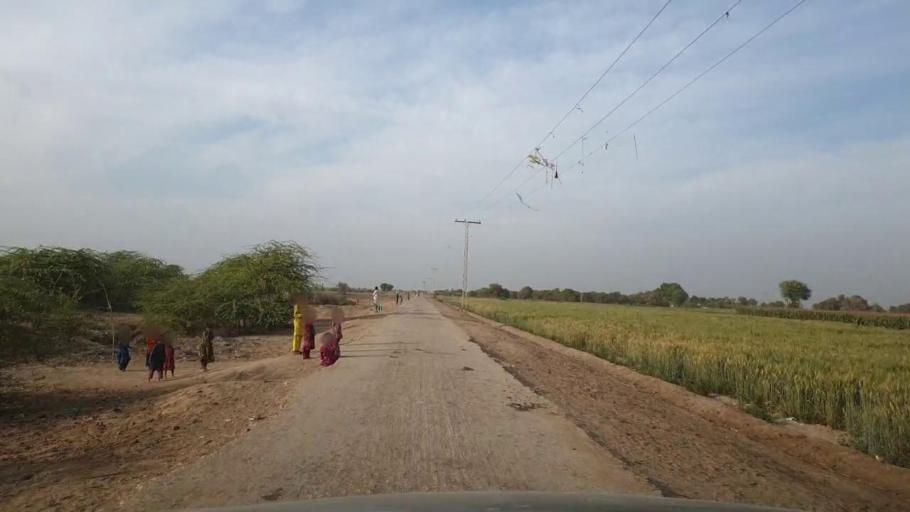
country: PK
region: Sindh
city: Kunri
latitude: 25.1983
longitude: 69.5199
